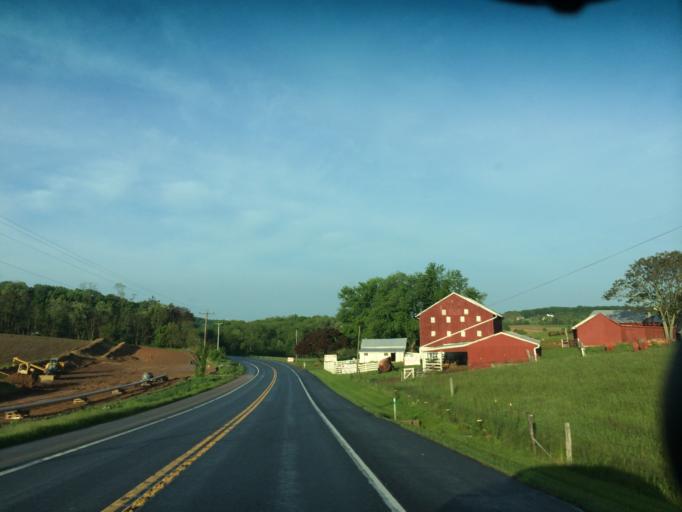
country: US
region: Maryland
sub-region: Carroll County
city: New Windsor
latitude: 39.5083
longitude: -77.0462
